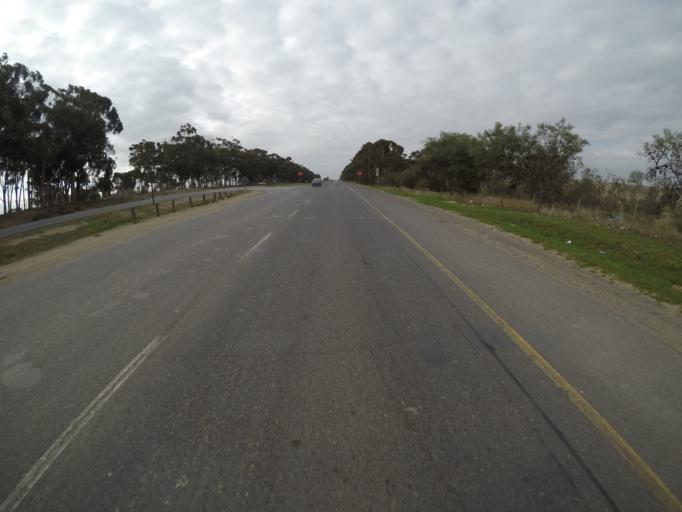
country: ZA
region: Western Cape
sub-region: City of Cape Town
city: Sunset Beach
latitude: -33.7752
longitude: 18.5486
